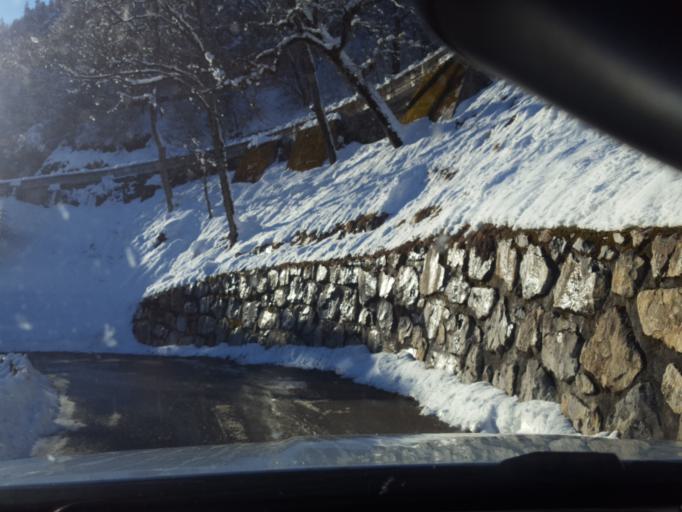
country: FR
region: Rhone-Alpes
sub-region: Departement de la Savoie
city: Salins-les-Thermes
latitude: 45.4598
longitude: 6.5094
